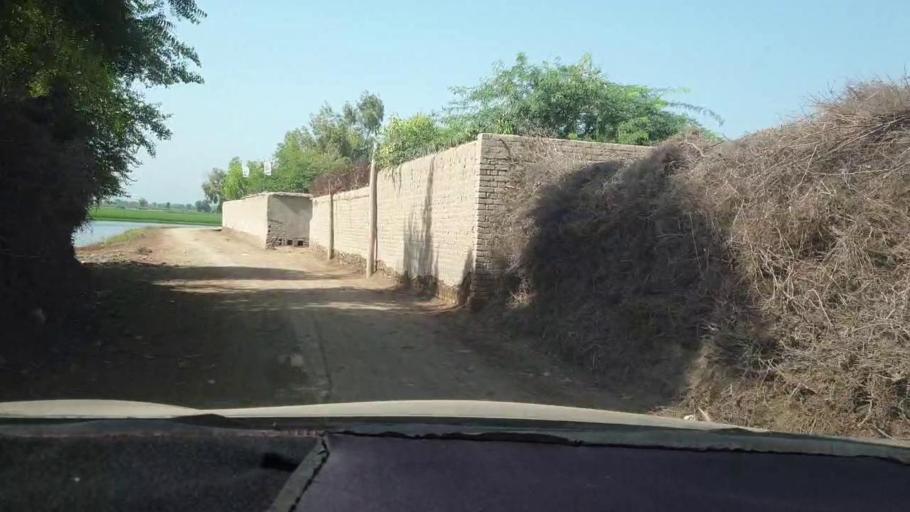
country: PK
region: Sindh
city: Miro Khan
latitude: 27.7055
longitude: 68.0936
